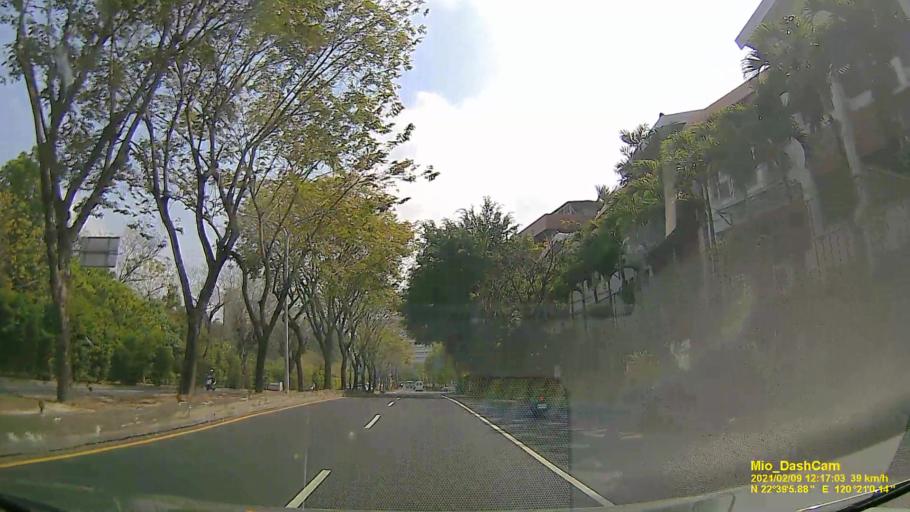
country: TW
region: Taiwan
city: Fengshan
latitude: 22.6516
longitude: 120.3501
